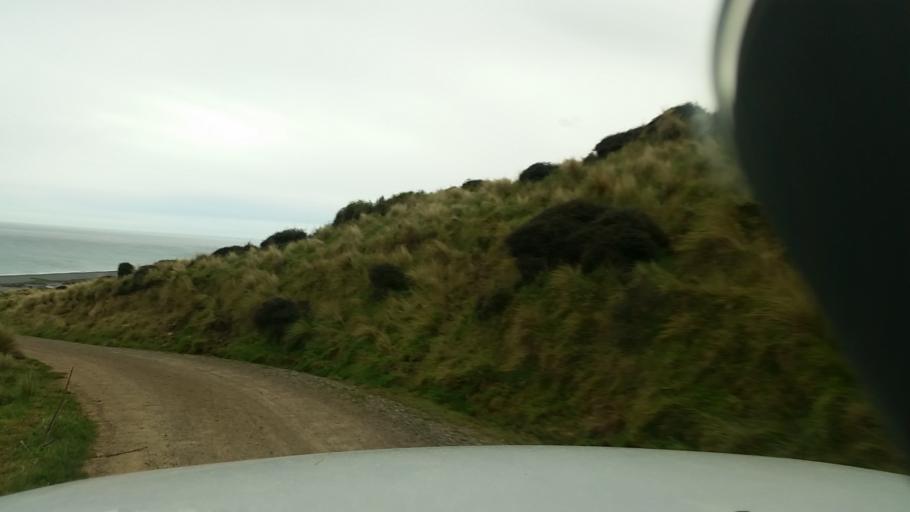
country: NZ
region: Canterbury
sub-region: Selwyn District
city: Lincoln
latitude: -43.8217
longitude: 172.7166
